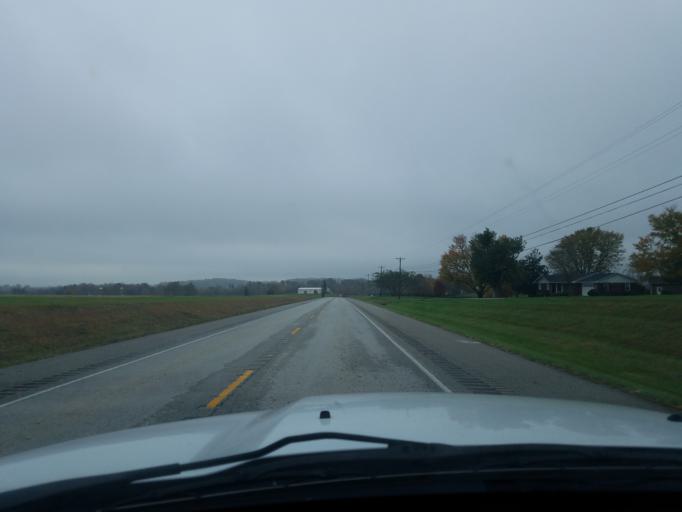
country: US
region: Kentucky
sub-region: Taylor County
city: Campbellsville
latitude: 37.3657
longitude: -85.3925
